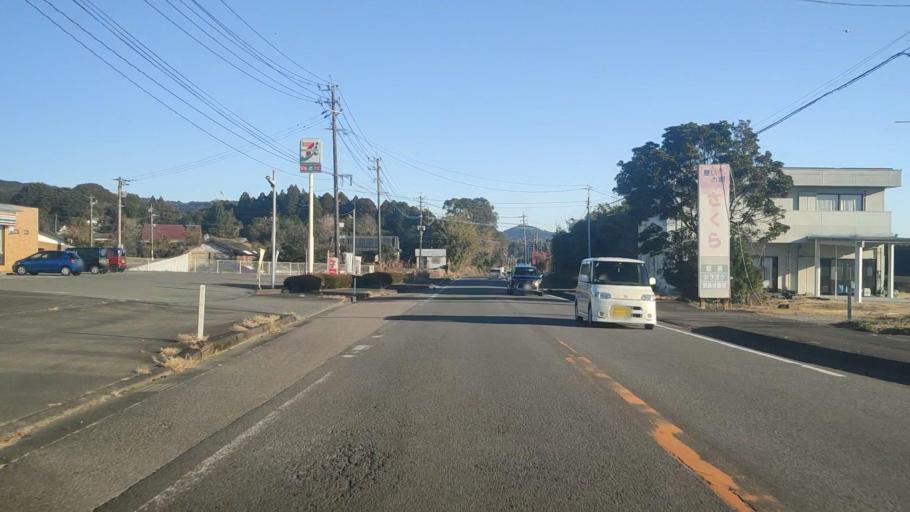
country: JP
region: Miyazaki
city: Takanabe
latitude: 32.3040
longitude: 131.5821
